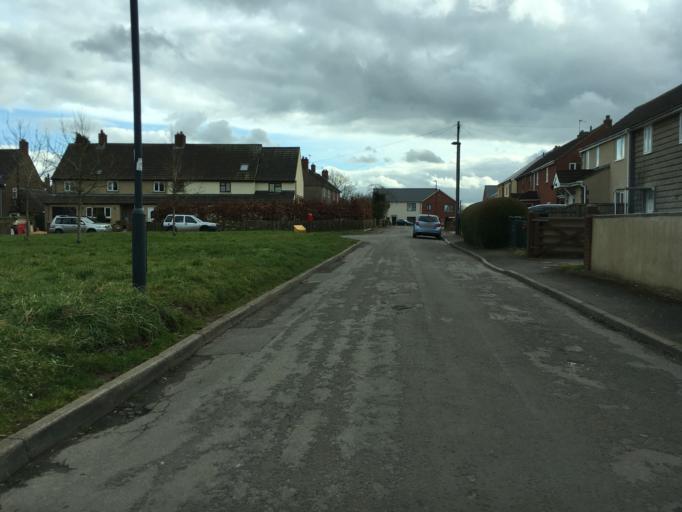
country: GB
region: England
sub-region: South Gloucestershire
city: Yate
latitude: 51.5475
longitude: -2.4604
